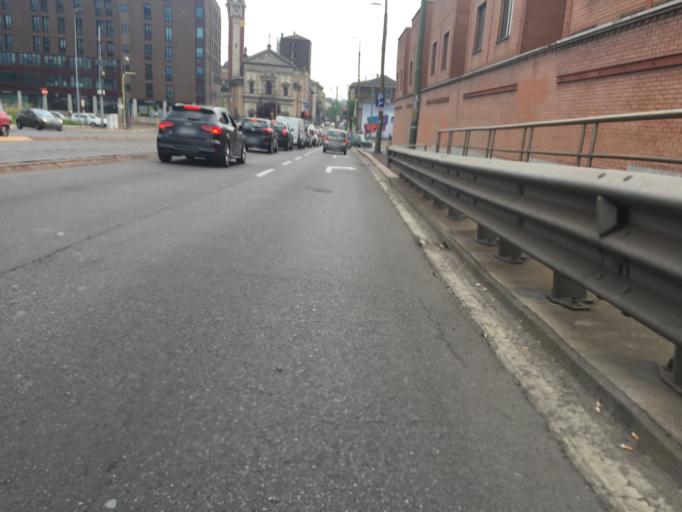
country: IT
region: Lombardy
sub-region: Citta metropolitana di Milano
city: Milano
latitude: 45.4866
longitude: 9.1821
